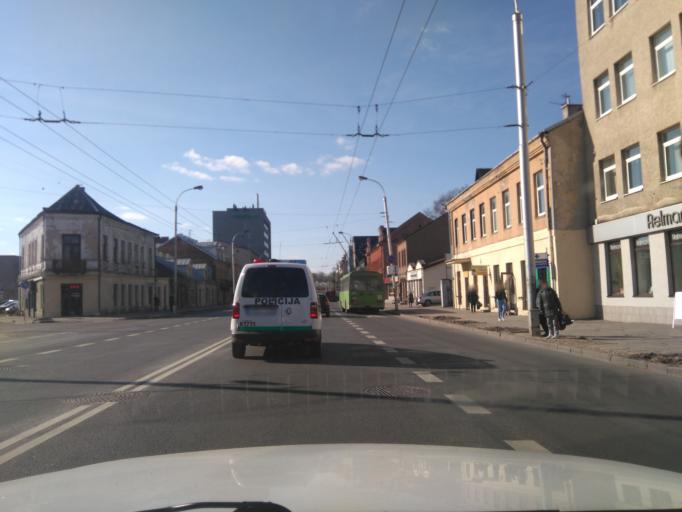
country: LT
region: Kauno apskritis
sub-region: Kaunas
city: Aleksotas
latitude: 54.8881
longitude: 23.9289
